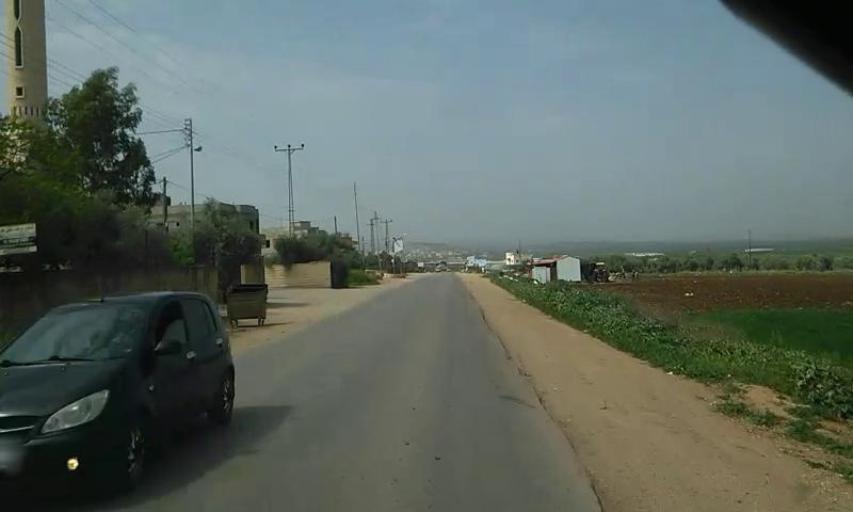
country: PS
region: West Bank
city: Kafr Dan
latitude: 32.4971
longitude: 35.2525
